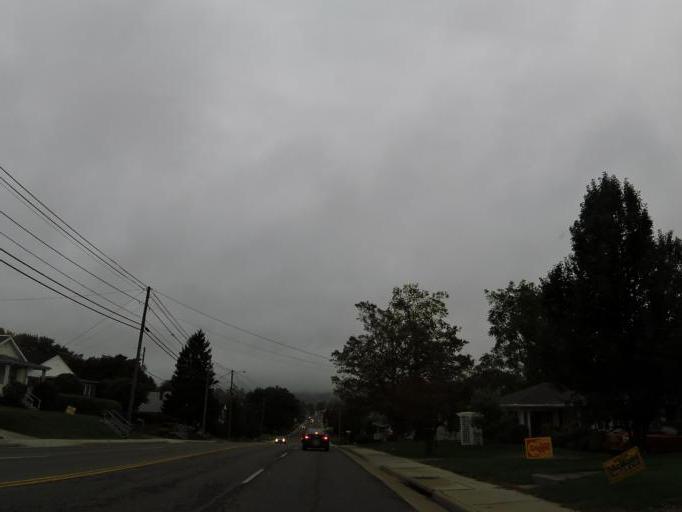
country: US
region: Virginia
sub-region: Wythe County
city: Wytheville
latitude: 36.9532
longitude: -81.0907
